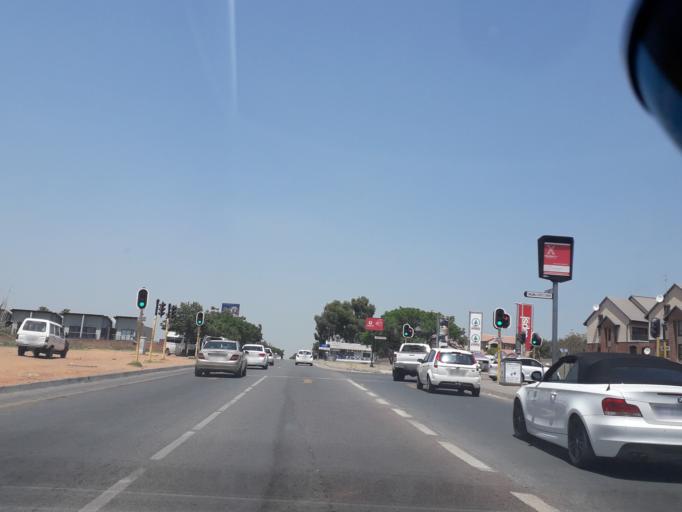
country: ZA
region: Gauteng
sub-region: City of Johannesburg Metropolitan Municipality
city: Midrand
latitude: -25.9798
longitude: 28.1181
